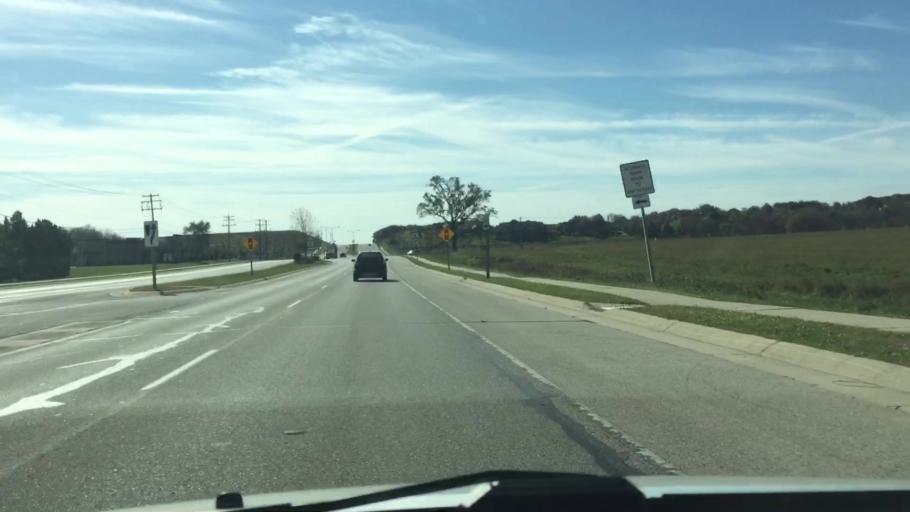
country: US
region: Wisconsin
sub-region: Waukesha County
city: Sussex
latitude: 43.1152
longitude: -88.2447
